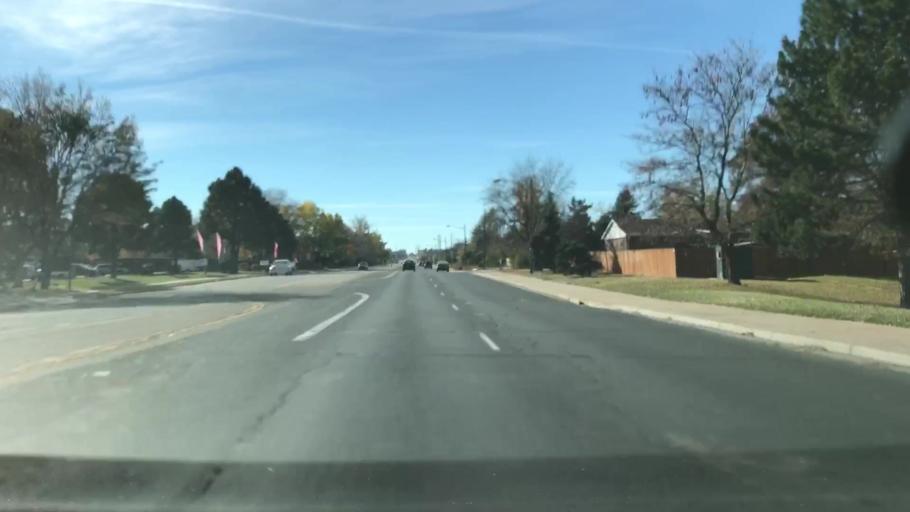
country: US
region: Colorado
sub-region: Arapahoe County
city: Glendale
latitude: 39.6934
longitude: -104.9035
